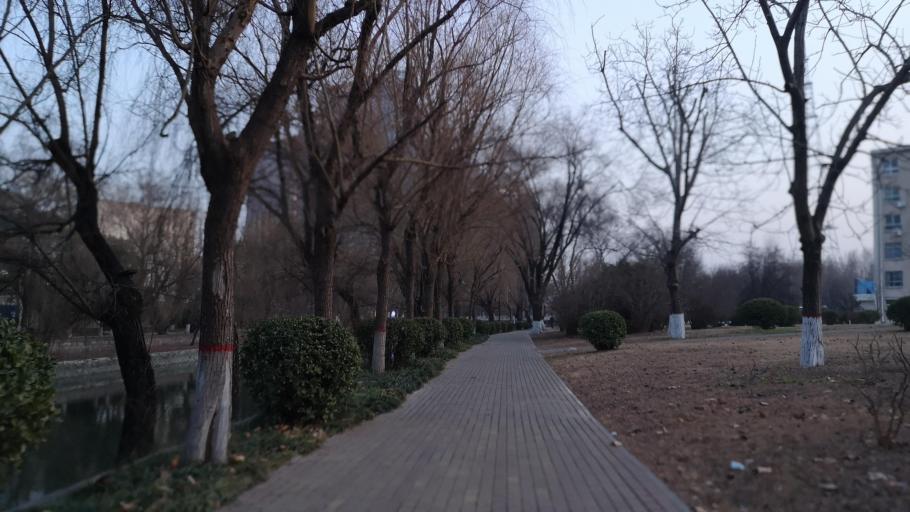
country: CN
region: Henan Sheng
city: Zhongyuanlu
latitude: 35.7771
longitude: 115.0776
